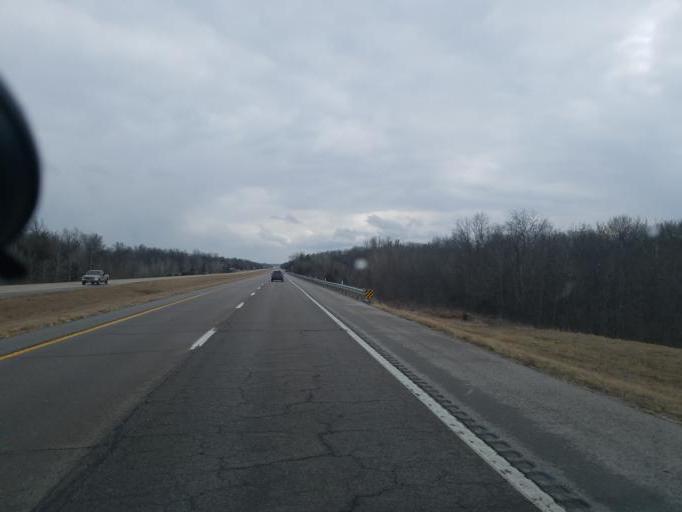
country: US
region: Missouri
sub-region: Boone County
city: Hallsville
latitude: 39.0851
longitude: -92.3300
